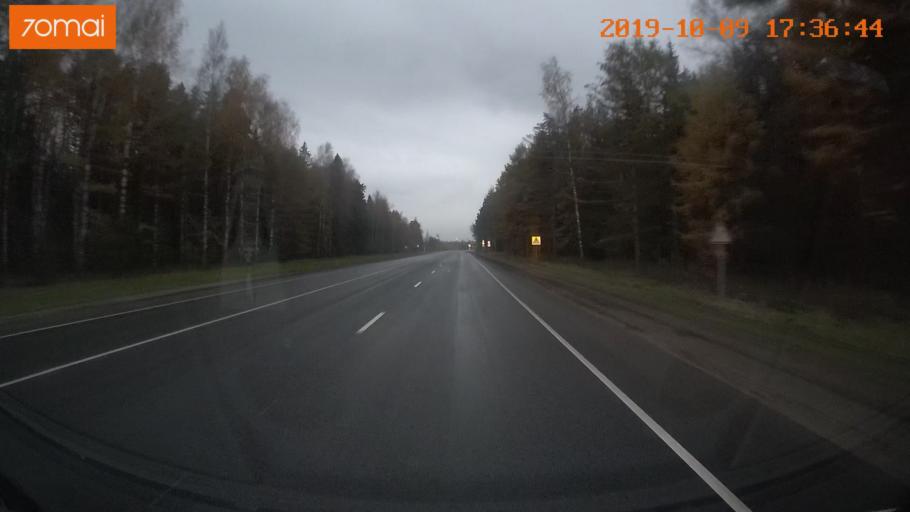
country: RU
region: Ivanovo
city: Bogorodskoye
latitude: 57.0744
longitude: 40.9933
